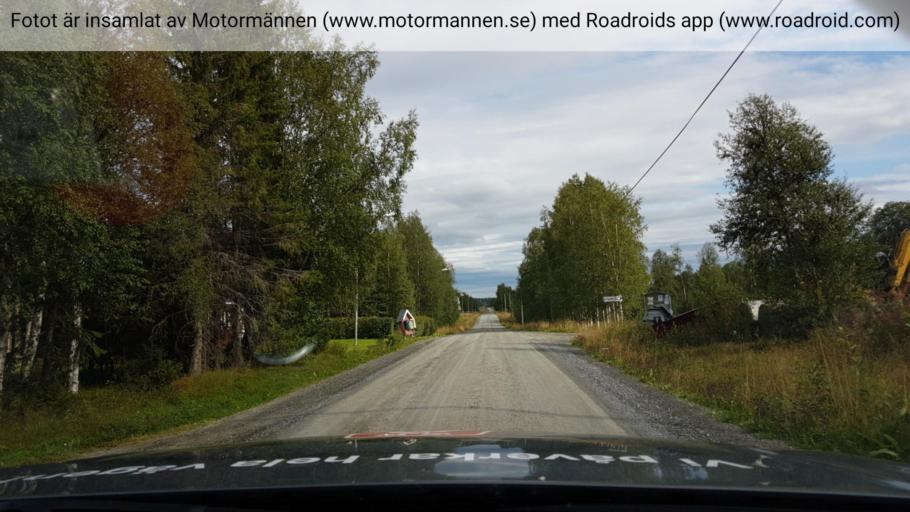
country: SE
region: Jaemtland
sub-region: Krokoms Kommun
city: Valla
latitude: 63.6970
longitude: 13.6250
